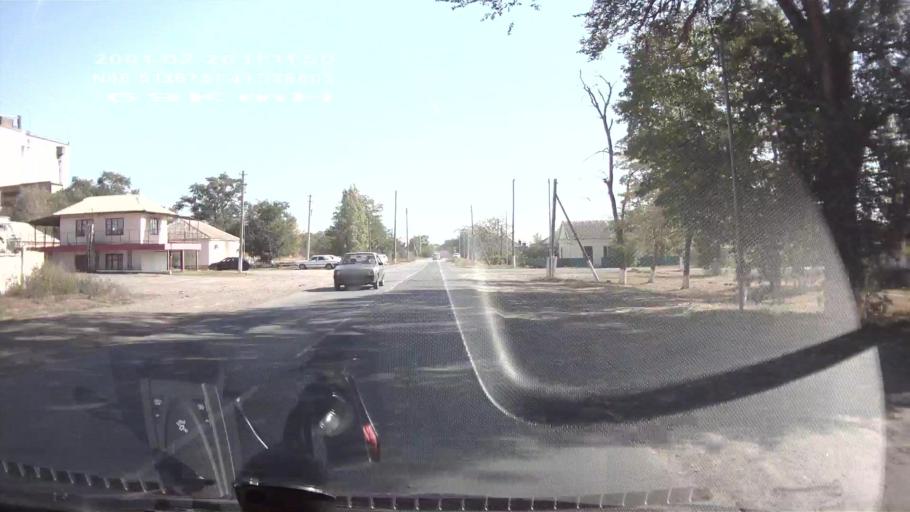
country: RU
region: Rostov
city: Gigant
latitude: 46.5137
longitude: 41.3358
